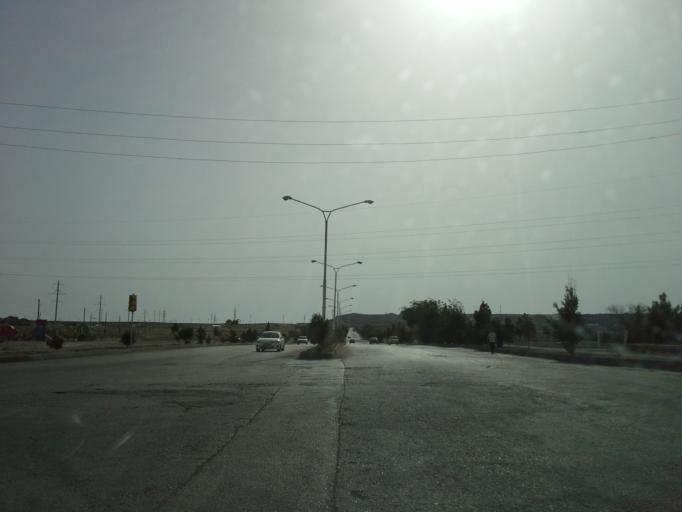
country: TM
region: Balkan
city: Turkmenbasy
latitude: 40.0407
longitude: 52.9909
